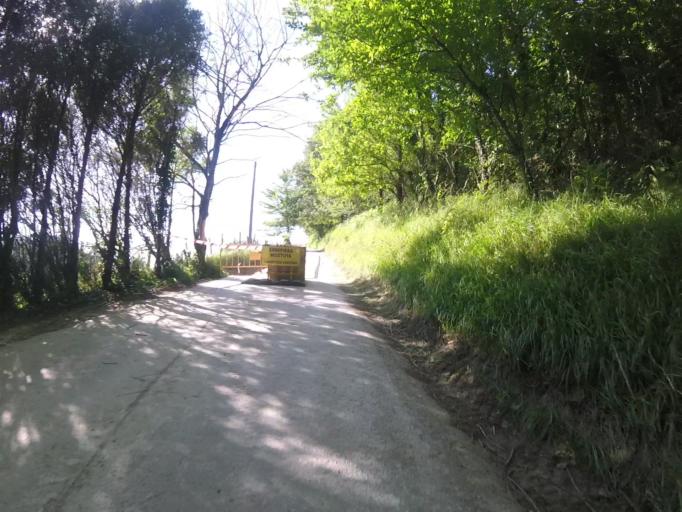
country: ES
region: Basque Country
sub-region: Provincia de Guipuzcoa
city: Astigarraga
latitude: 43.2952
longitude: -1.9328
